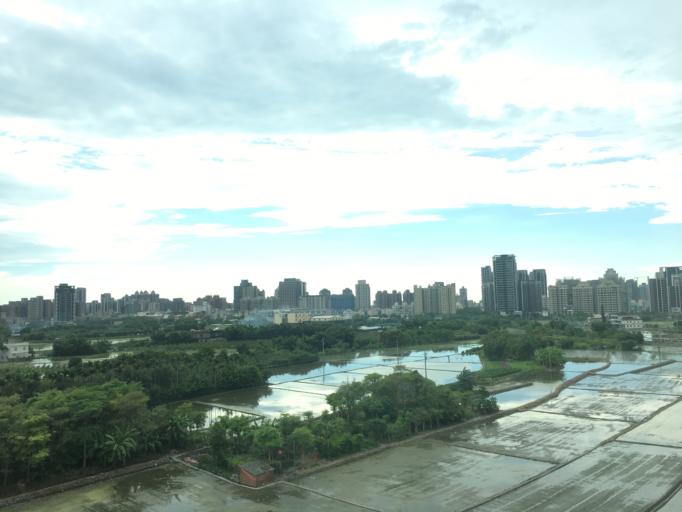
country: TW
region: Taiwan
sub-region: Hsinchu
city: Zhubei
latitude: 24.8184
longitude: 121.0428
